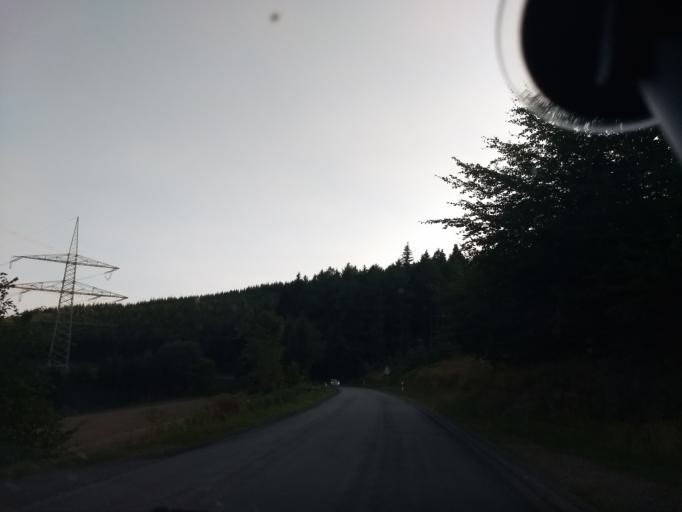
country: DE
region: North Rhine-Westphalia
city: Eslohe
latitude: 51.2662
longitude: 8.0823
